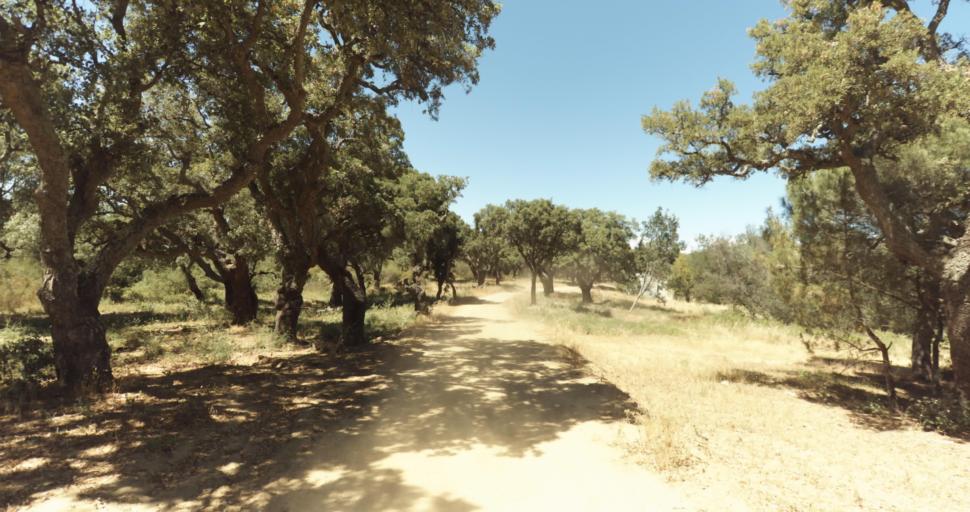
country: FR
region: Provence-Alpes-Cote d'Azur
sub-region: Departement du Var
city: Gassin
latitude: 43.2524
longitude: 6.5644
